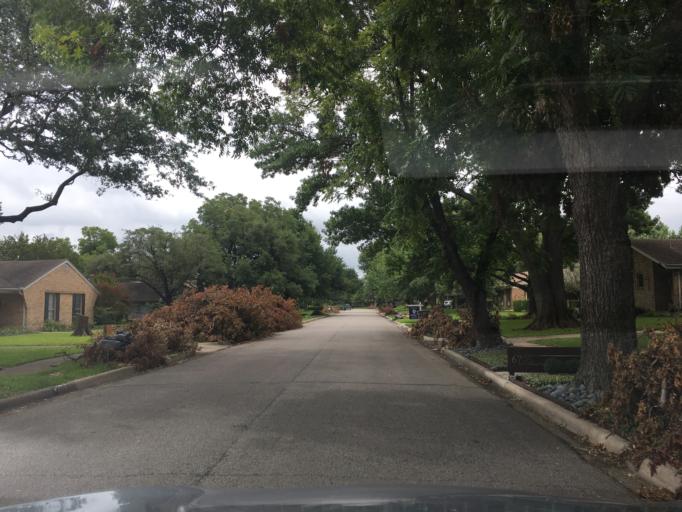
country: US
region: Texas
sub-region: Dallas County
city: Highland Park
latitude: 32.8585
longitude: -96.7448
